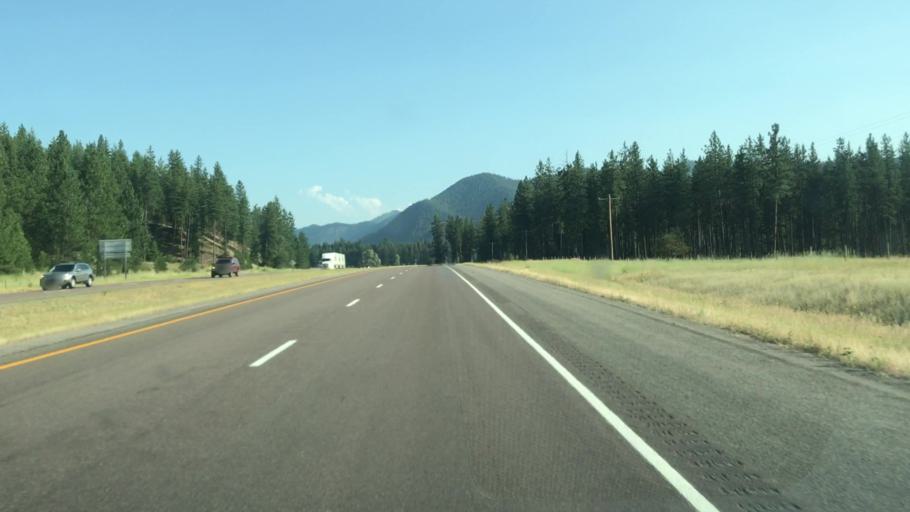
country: US
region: Montana
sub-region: Mineral County
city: Superior
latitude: 47.0629
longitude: -114.7637
